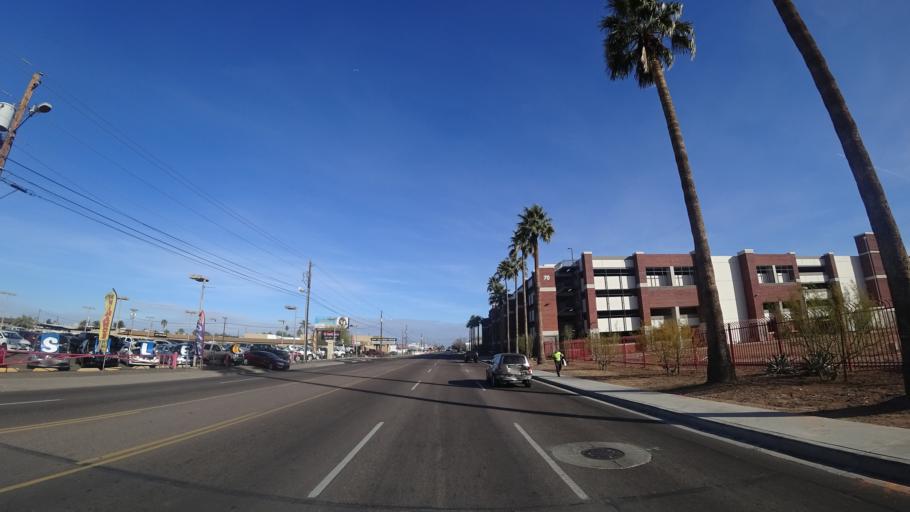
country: US
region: Arizona
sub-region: Maricopa County
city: Glendale
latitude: 33.5115
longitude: -112.1169
